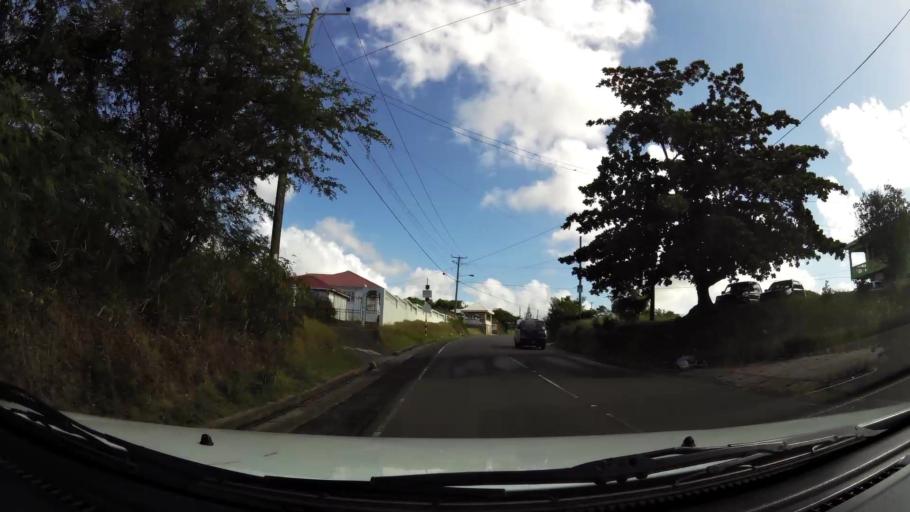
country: LC
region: Choiseul Quarter
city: Choiseul
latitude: 13.7717
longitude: -61.0456
